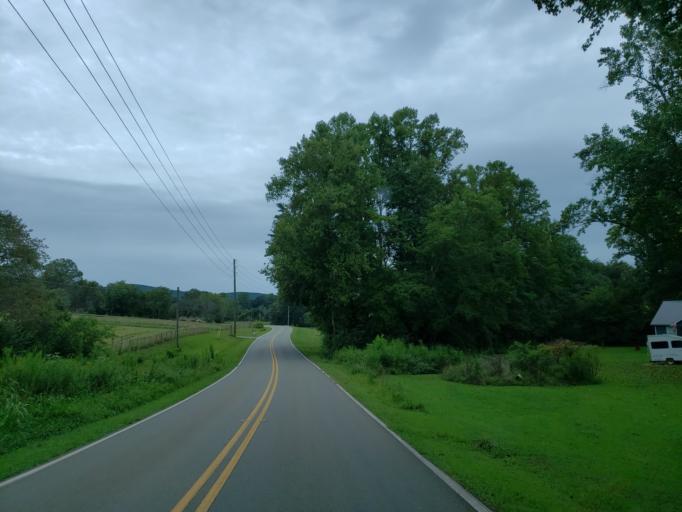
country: US
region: Georgia
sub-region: Pickens County
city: Jasper
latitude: 34.4157
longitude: -84.5747
